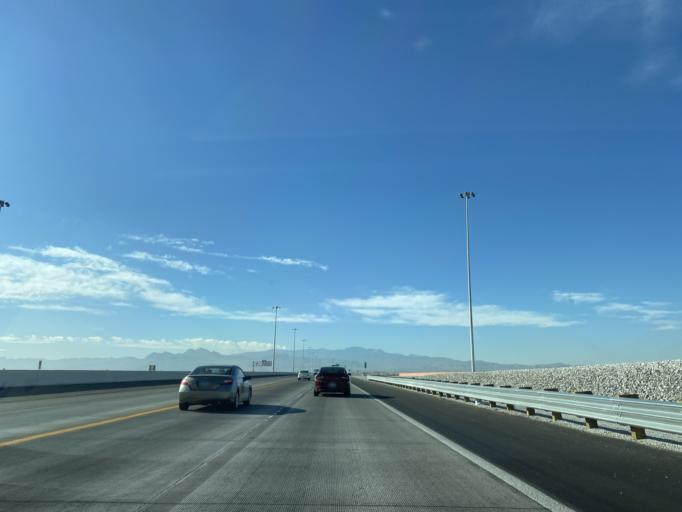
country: US
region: Nevada
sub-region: Clark County
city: Nellis Air Force Base
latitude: 36.2899
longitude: -115.1007
